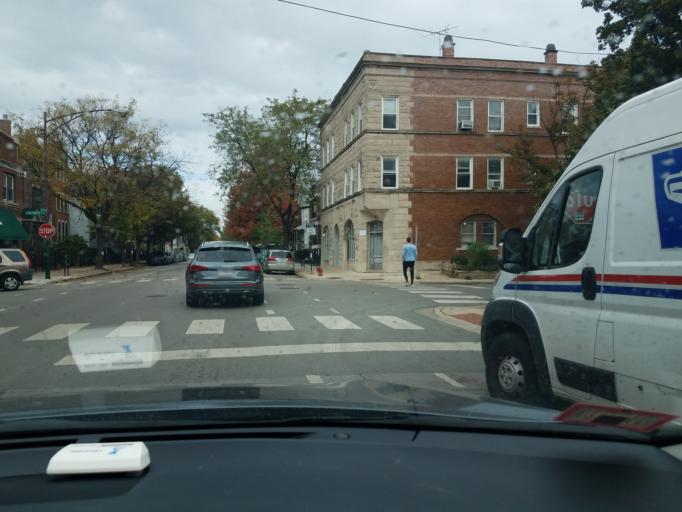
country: US
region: Illinois
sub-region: Cook County
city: Chicago
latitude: 41.9269
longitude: -87.6633
